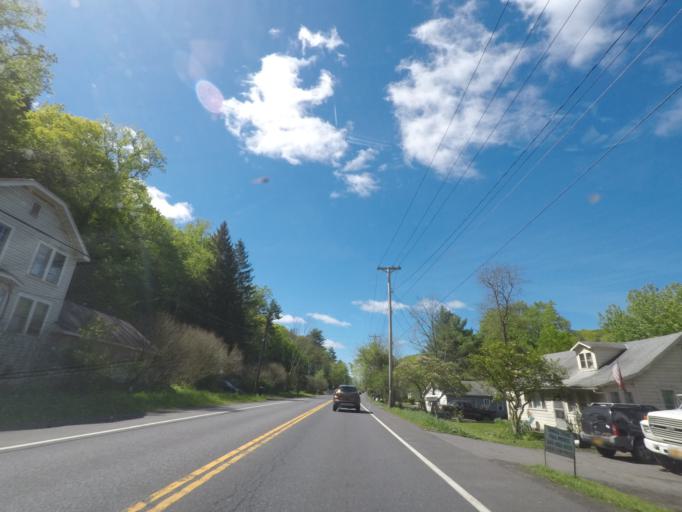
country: US
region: New York
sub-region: Ulster County
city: Glasco
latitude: 42.0340
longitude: -73.9728
